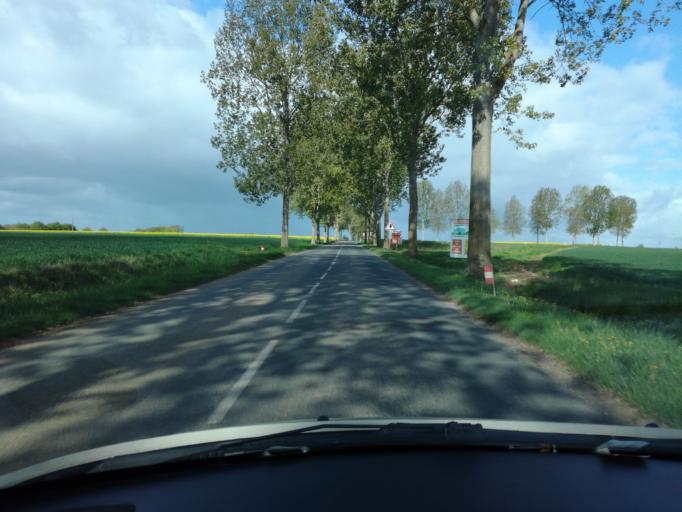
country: FR
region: Picardie
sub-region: Departement de la Somme
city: Hornoy-le-Bourg
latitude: 49.8541
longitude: 1.8628
